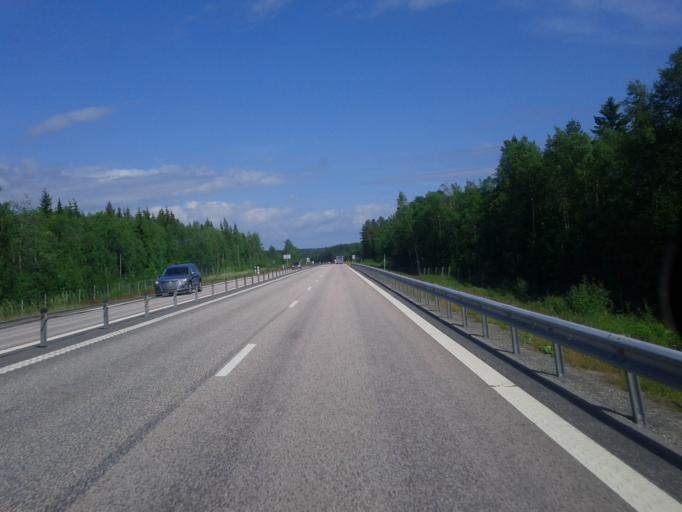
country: SE
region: Vaesternorrland
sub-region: OErnskoeldsviks Kommun
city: Husum
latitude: 63.3975
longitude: 19.1981
